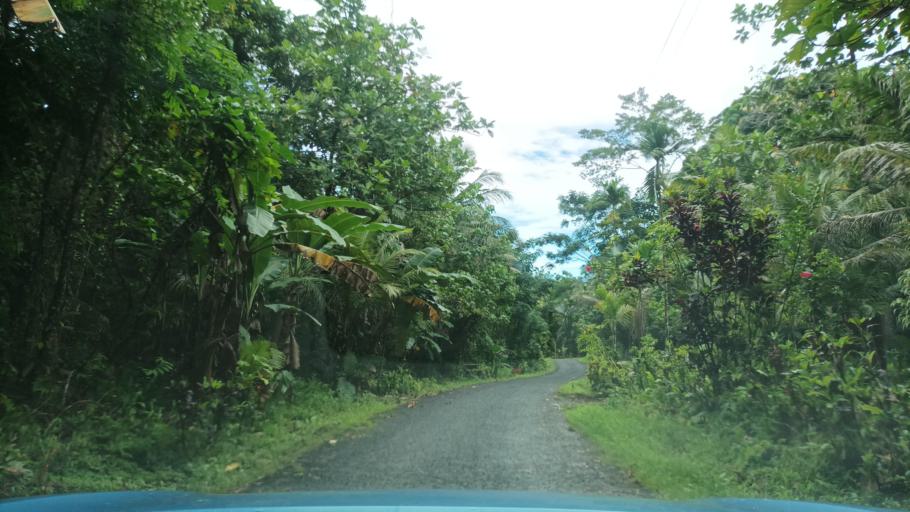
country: FM
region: Pohnpei
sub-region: Sokehs Municipality
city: Palikir - National Government Center
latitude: 6.8372
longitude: 158.1751
